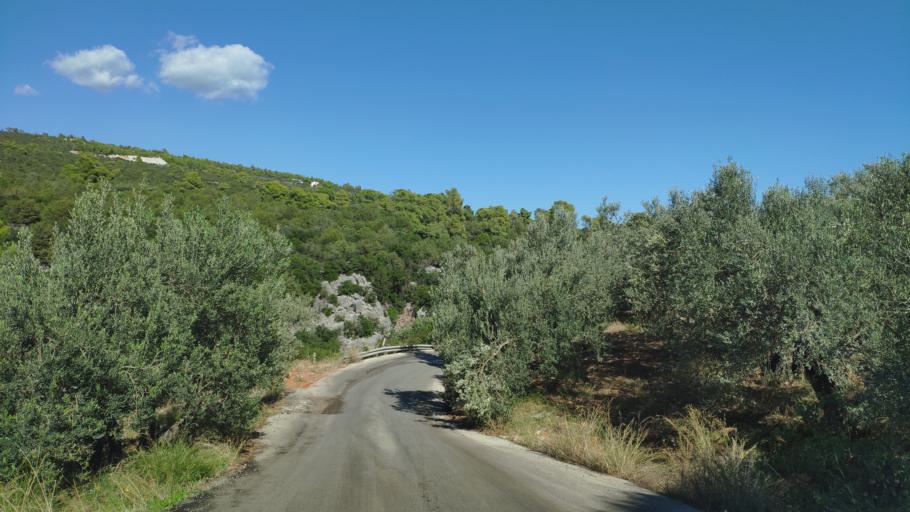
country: GR
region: Peloponnese
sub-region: Nomos Korinthias
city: Sofikon
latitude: 37.7341
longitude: 23.1046
